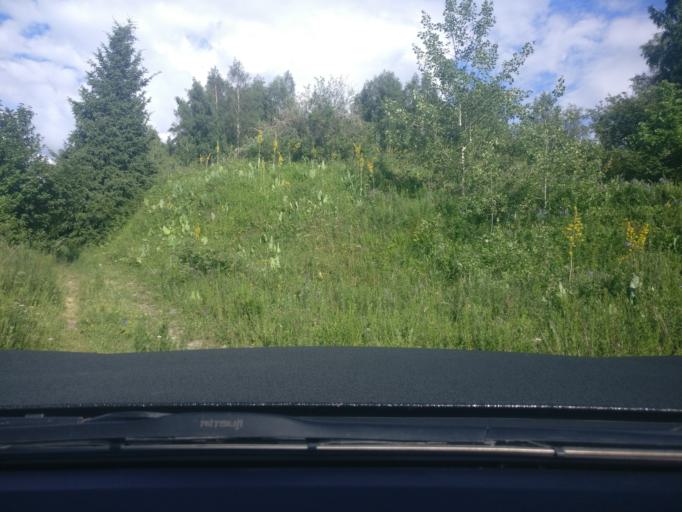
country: KZ
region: Almaty Qalasy
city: Almaty
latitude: 43.1154
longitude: 76.9302
